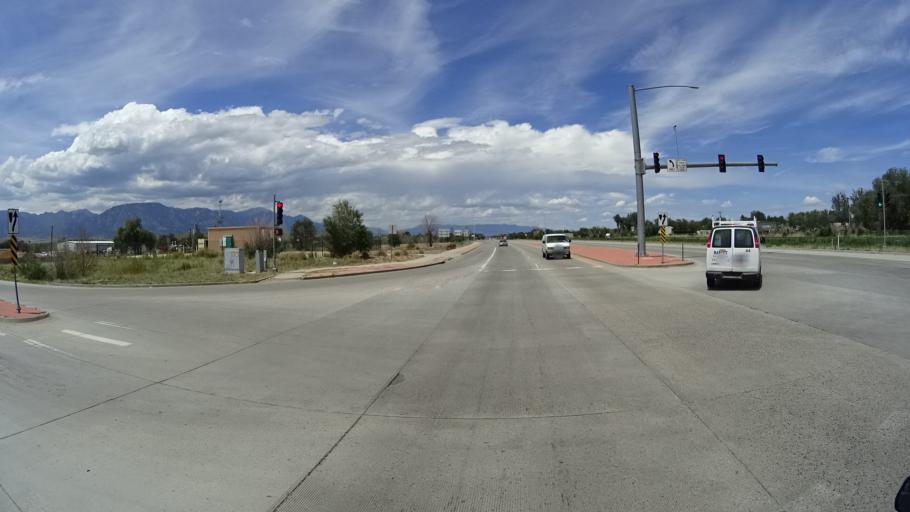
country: US
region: Colorado
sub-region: El Paso County
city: Security-Widefield
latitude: 38.7246
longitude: -104.7197
